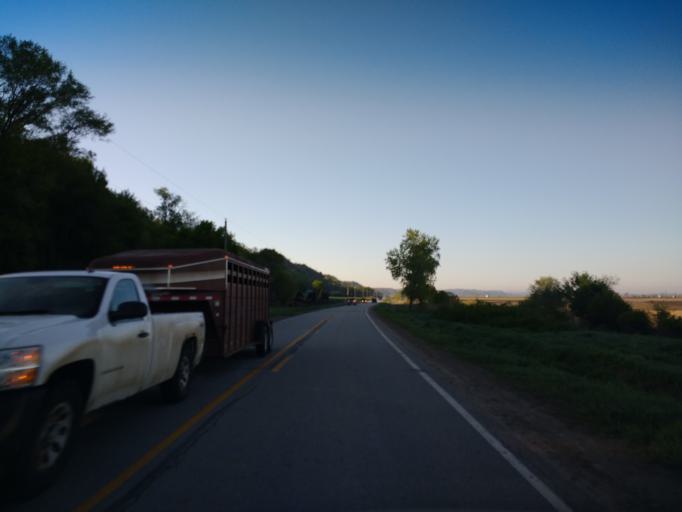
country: US
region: Iowa
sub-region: Harrison County
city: Missouri Valley
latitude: 41.4844
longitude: -95.8854
